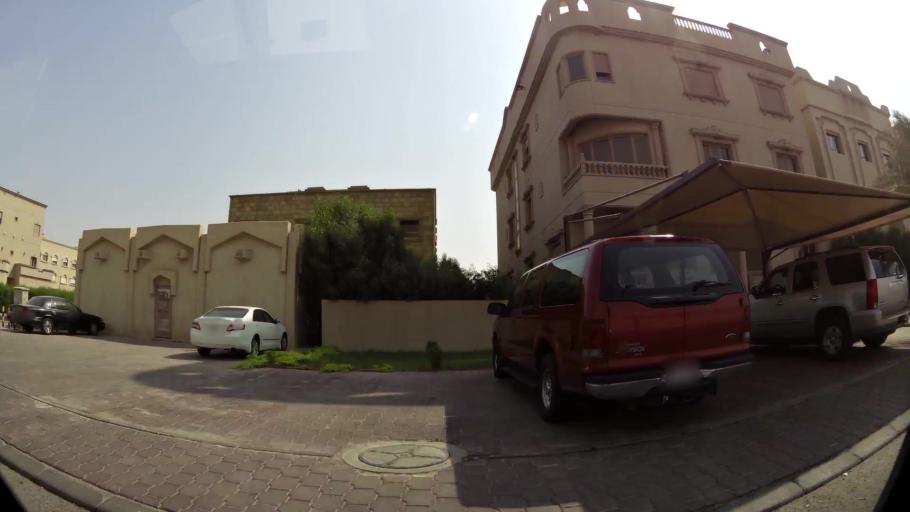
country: KW
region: Muhafazat al Jahra'
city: Al Jahra'
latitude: 29.3255
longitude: 47.7379
